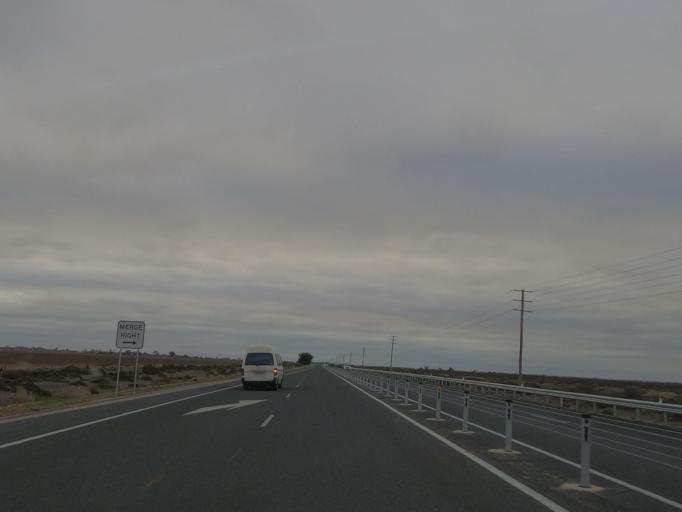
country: AU
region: Victoria
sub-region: Swan Hill
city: Swan Hill
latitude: -35.5074
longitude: 143.7215
